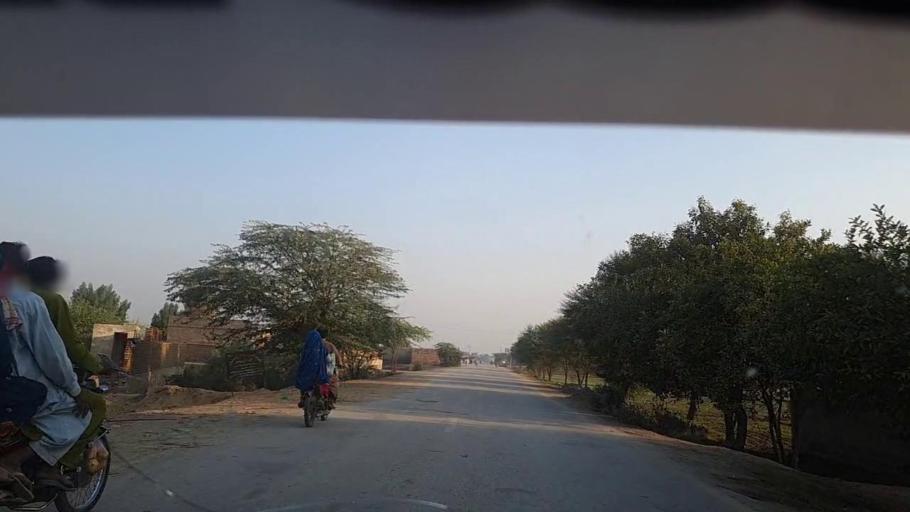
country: PK
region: Sindh
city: Ranipur
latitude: 27.2671
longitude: 68.5205
